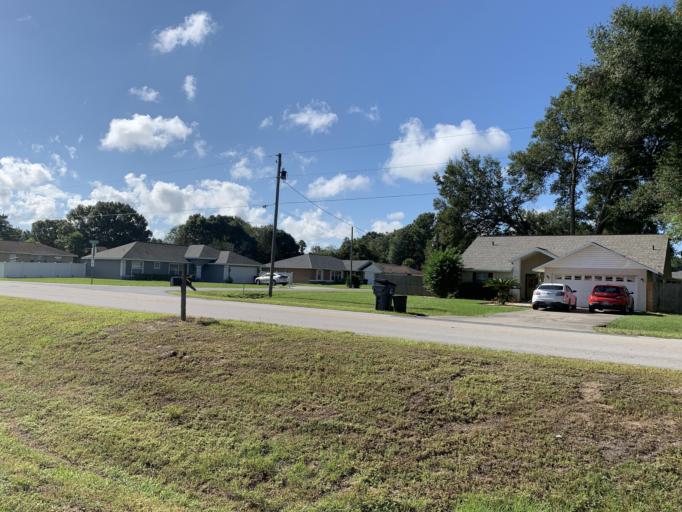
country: US
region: Florida
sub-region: Marion County
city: Silver Springs Shores
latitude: 29.1586
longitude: -82.0487
